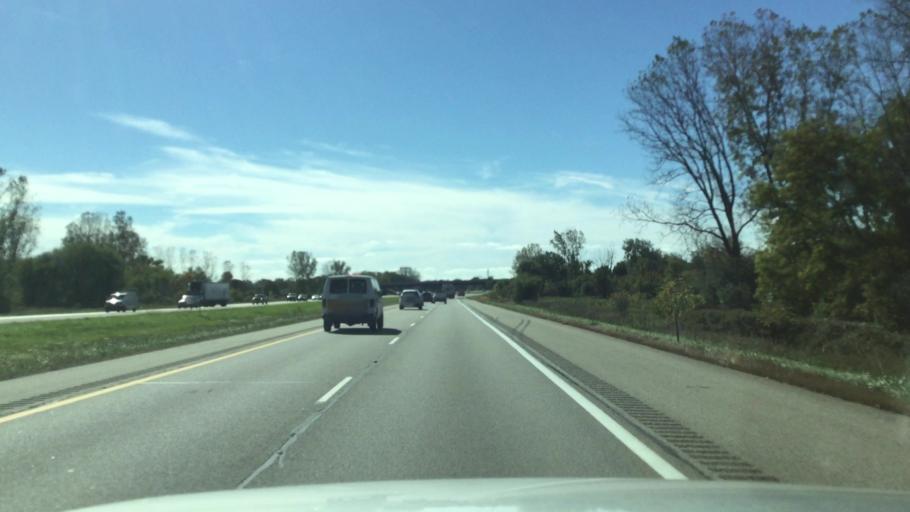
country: US
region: Michigan
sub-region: Washtenaw County
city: Ypsilanti
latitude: 42.3298
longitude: -83.6257
